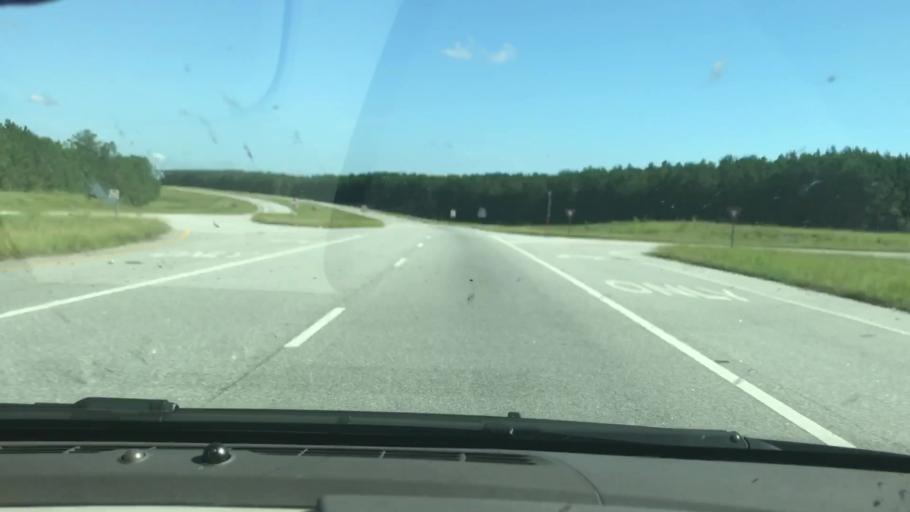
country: US
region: Alabama
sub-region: Russell County
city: Ladonia
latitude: 32.2119
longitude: -85.1690
